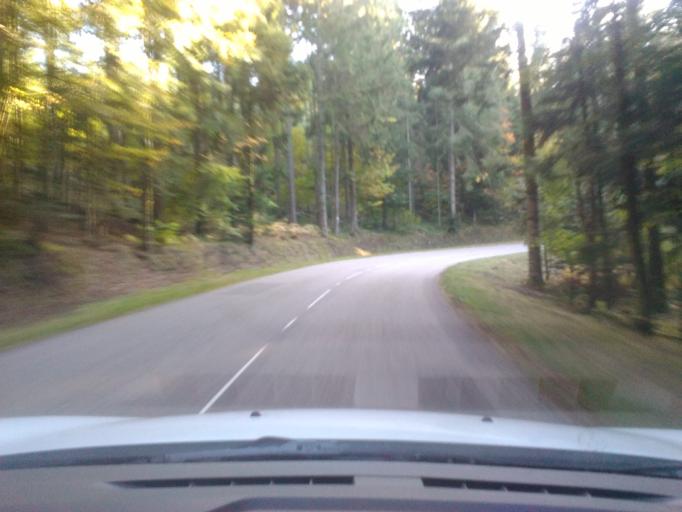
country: FR
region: Lorraine
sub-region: Departement des Vosges
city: Bruyeres
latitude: 48.2887
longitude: 6.7853
